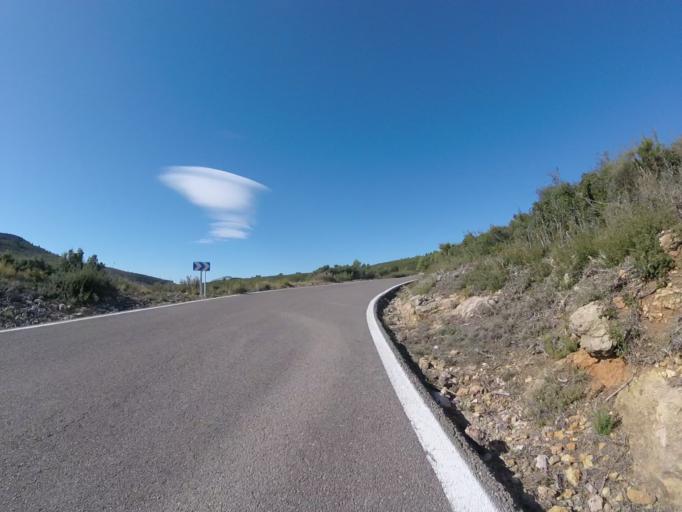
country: ES
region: Valencia
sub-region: Provincia de Castello
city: Albocasser
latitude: 40.3919
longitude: 0.0393
